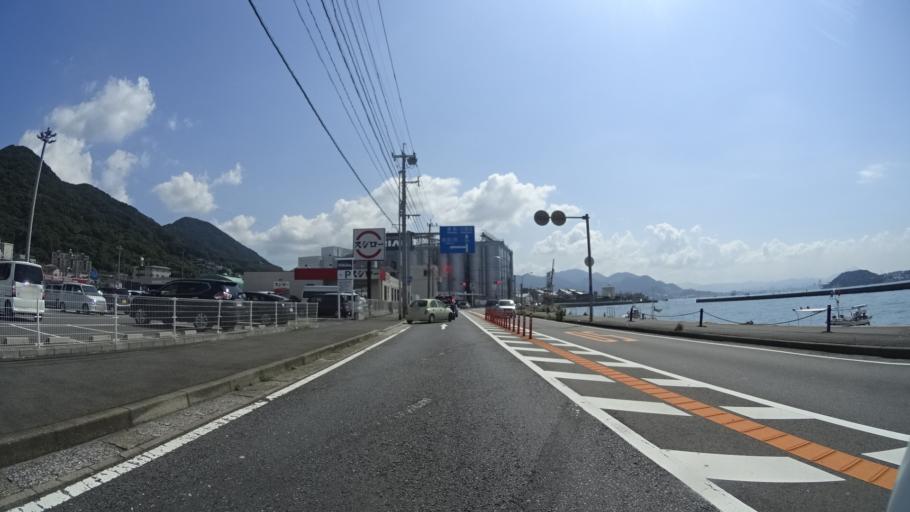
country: JP
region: Yamaguchi
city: Shimonoseki
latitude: 33.9271
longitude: 130.9420
